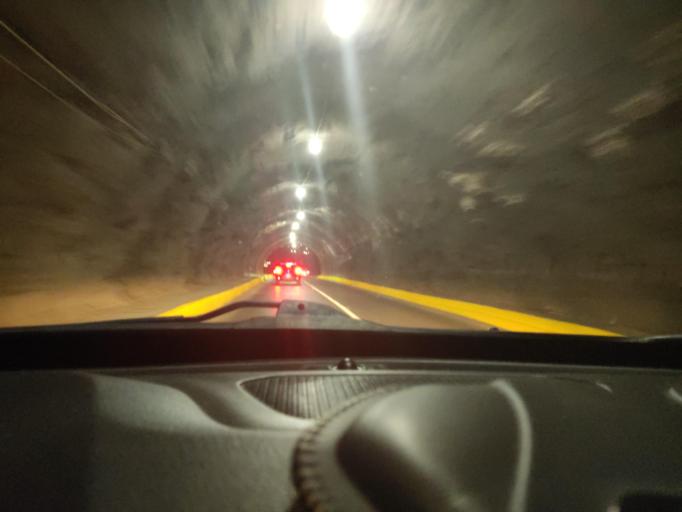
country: MX
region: Guanajuato
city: Marfil
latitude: 21.0038
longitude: -101.2707
